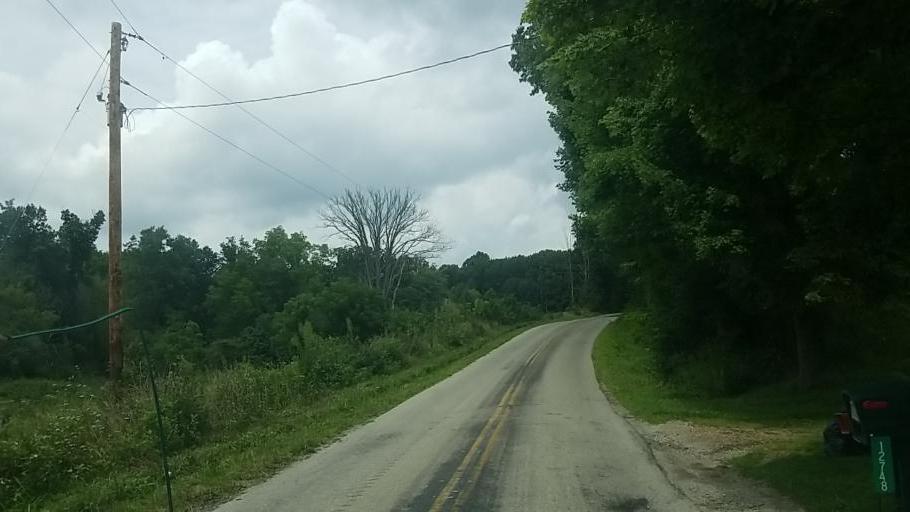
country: US
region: Ohio
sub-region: Licking County
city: Utica
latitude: 40.2346
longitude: -82.3367
